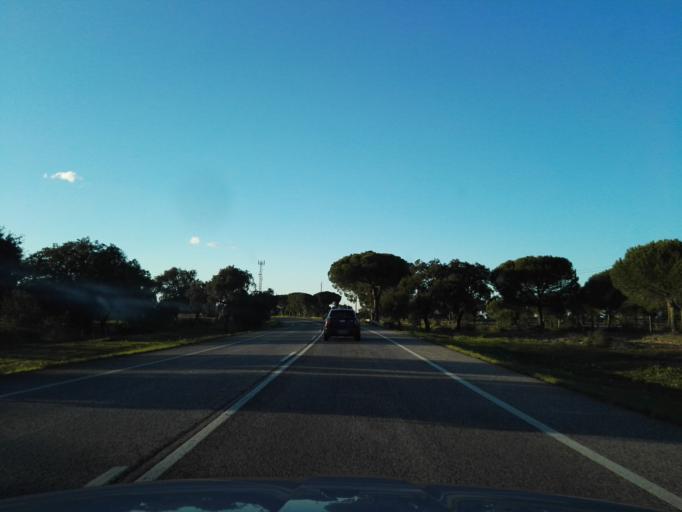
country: PT
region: Santarem
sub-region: Benavente
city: Poceirao
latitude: 38.8659
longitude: -8.7868
